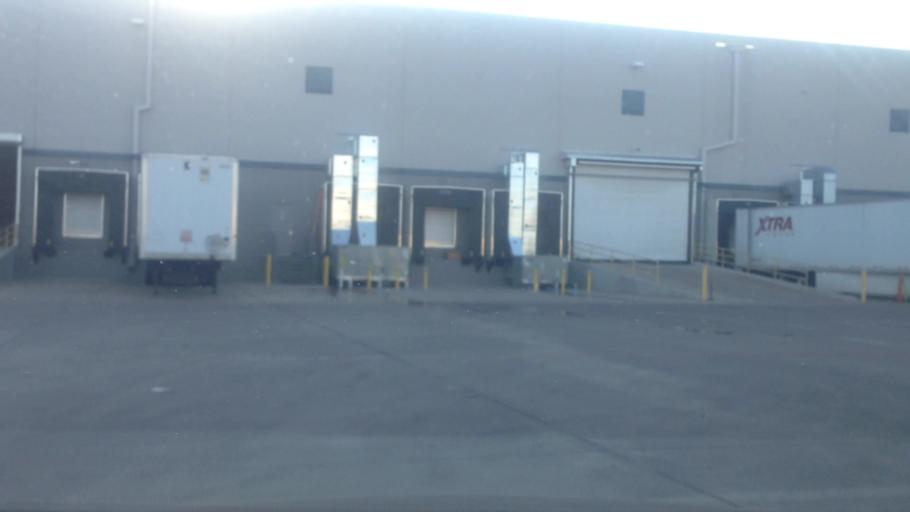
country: US
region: Texas
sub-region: Tarrant County
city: Blue Mound
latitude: 32.8282
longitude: -97.3532
